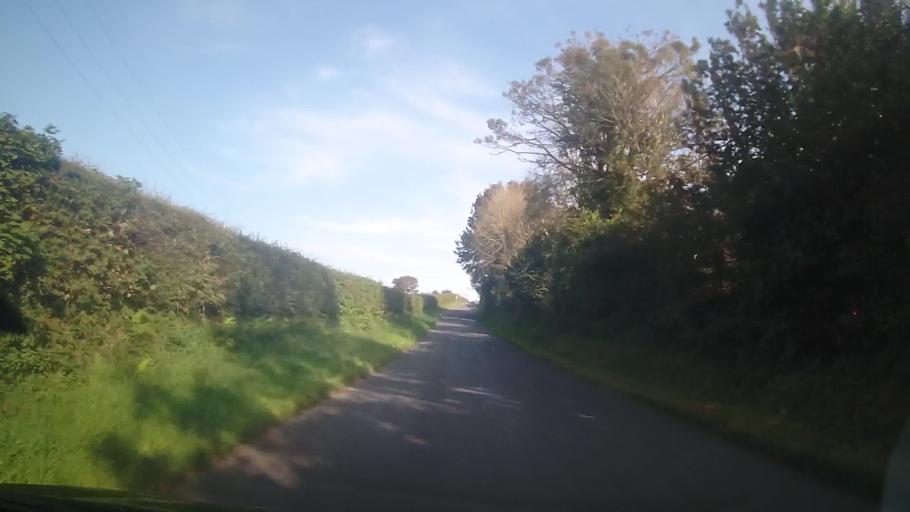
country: GB
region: Wales
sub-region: Pembrokeshire
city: Fishguard
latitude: 51.9837
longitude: -4.9498
